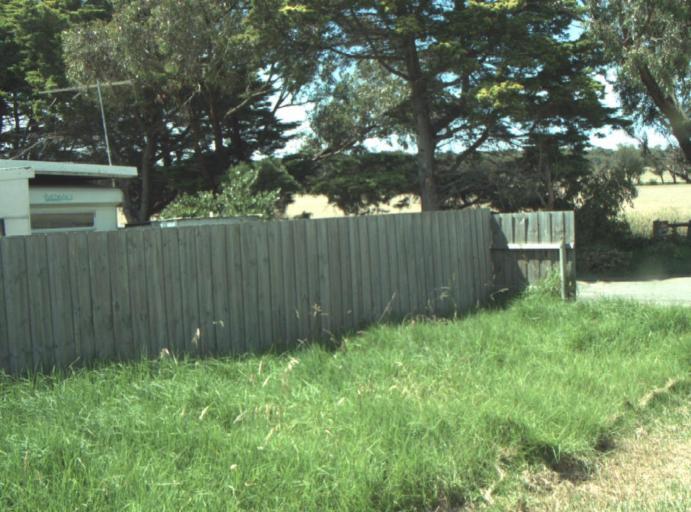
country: AU
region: Victoria
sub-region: Greater Geelong
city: Leopold
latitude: -38.1654
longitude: 144.4729
